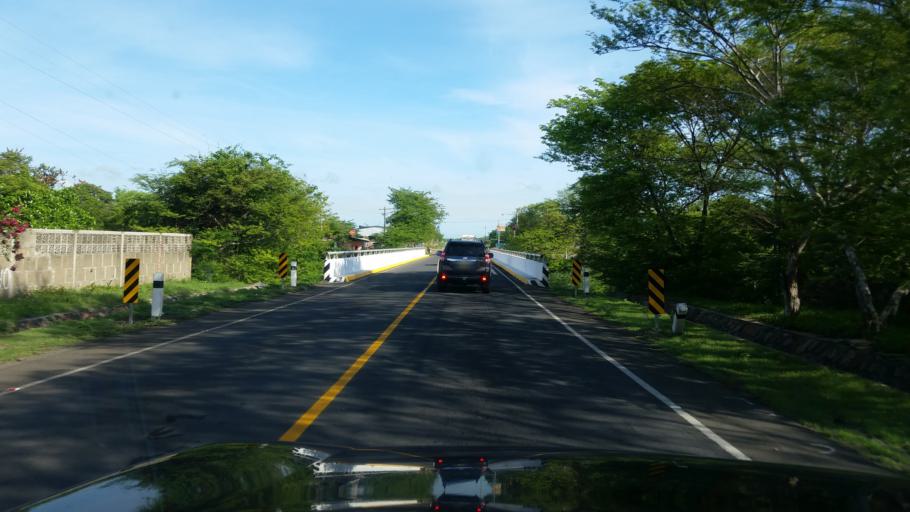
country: NI
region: Leon
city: La Paz Centro
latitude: 12.2423
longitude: -86.7153
